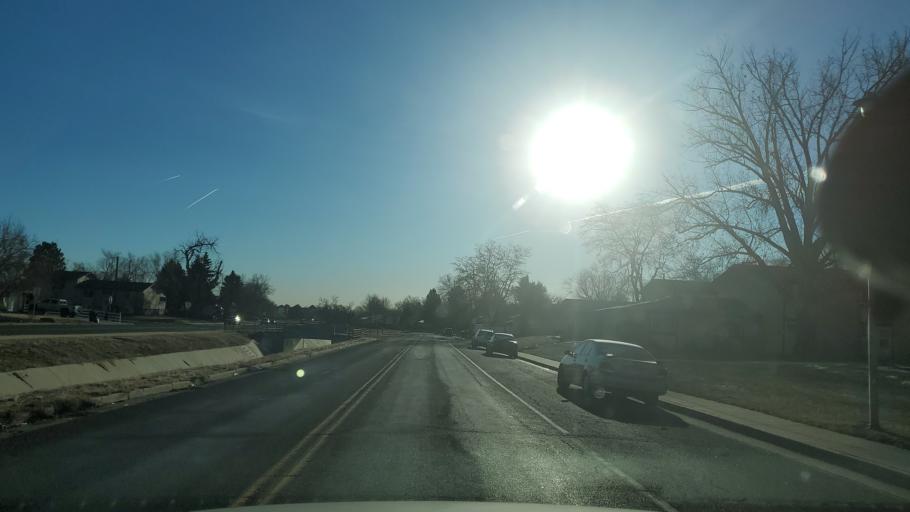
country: US
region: Colorado
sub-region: Adams County
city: Welby
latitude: 39.8456
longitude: -104.9743
